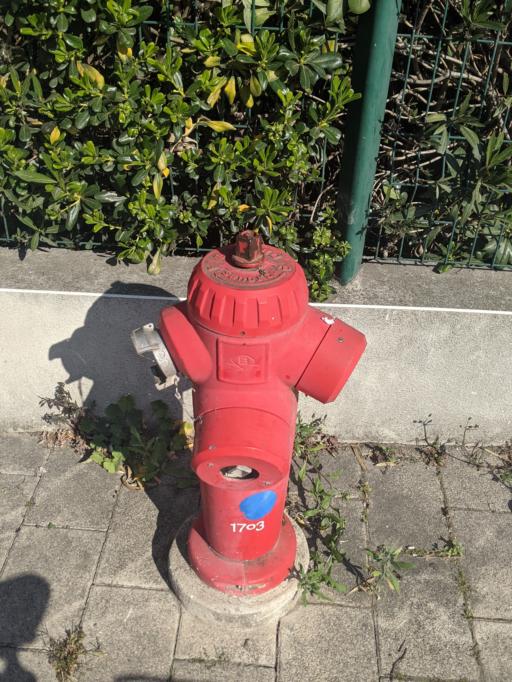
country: FR
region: Languedoc-Roussillon
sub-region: Departement de l'Herault
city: Montpellier
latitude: 43.5884
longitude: 3.8658
